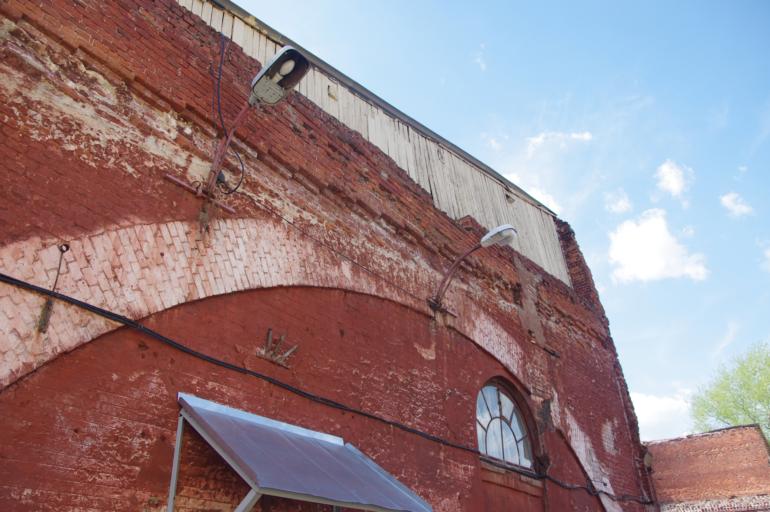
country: RU
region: Moskovskaya
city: Klin
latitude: 56.3324
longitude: 36.7092
